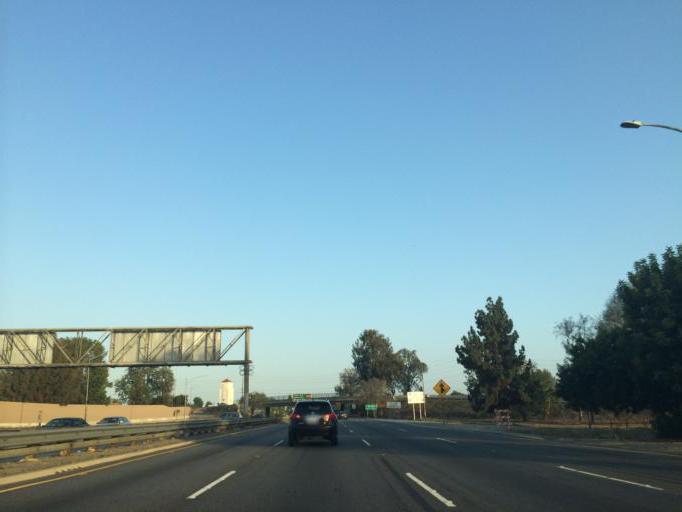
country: US
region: California
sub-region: Los Angeles County
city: Santa Fe Springs
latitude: 33.9375
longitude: -118.0942
